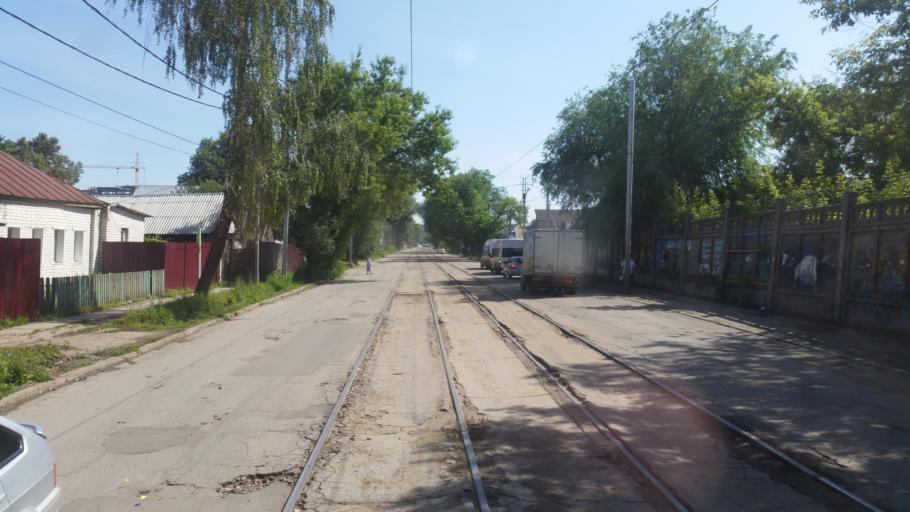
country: RU
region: Ulyanovsk
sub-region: Ulyanovskiy Rayon
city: Ulyanovsk
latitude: 54.3421
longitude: 48.3800
